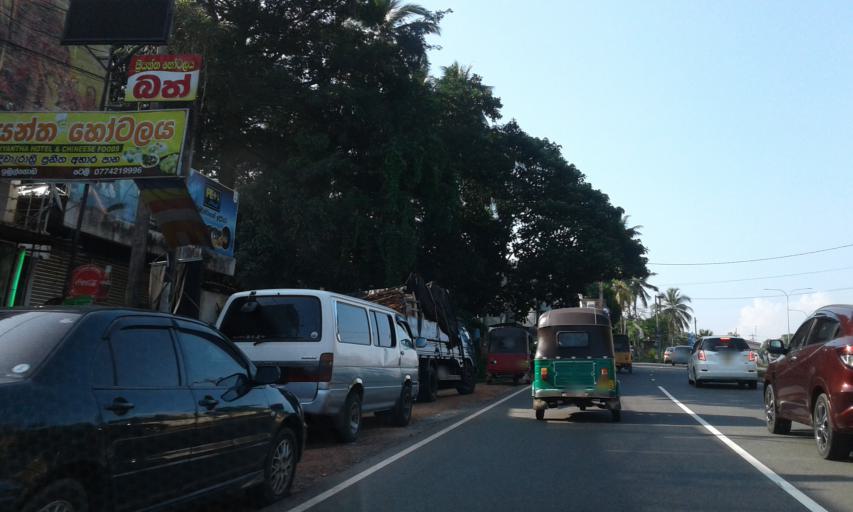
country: LK
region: Western
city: Gampaha
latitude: 7.0366
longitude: 79.9916
